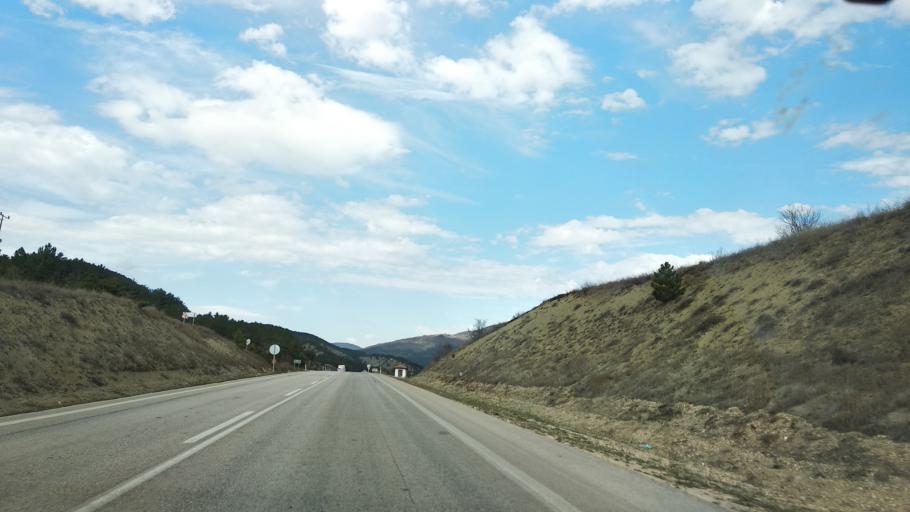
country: TR
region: Bolu
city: Mudurnu
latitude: 40.4574
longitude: 31.1586
